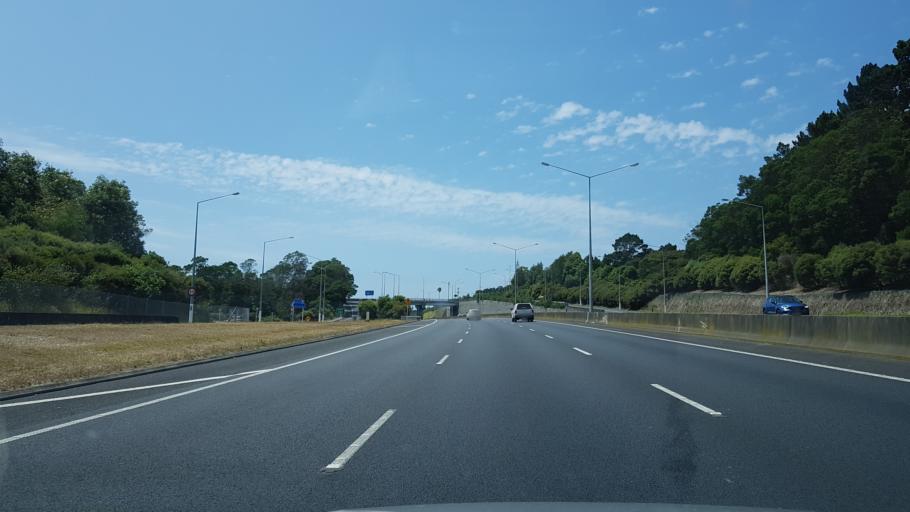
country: NZ
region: Auckland
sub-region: Auckland
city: North Shore
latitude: -36.7832
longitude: 174.6740
